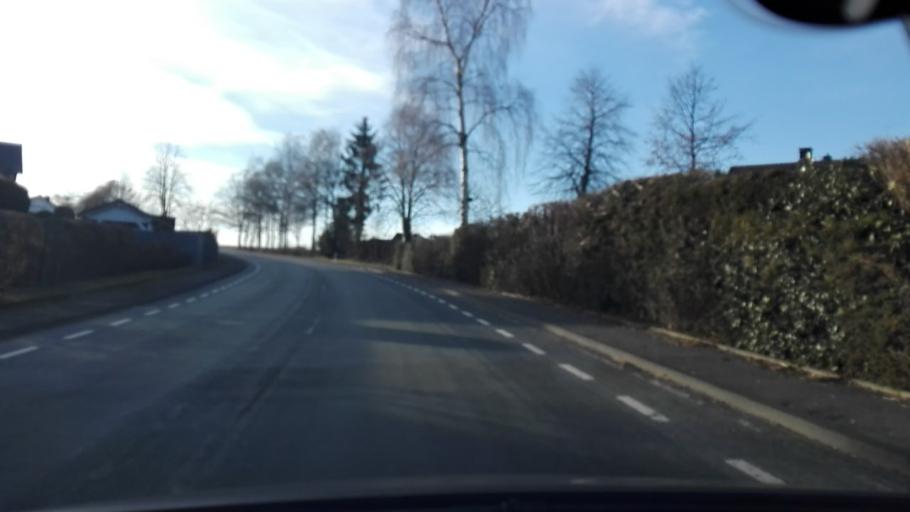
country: DE
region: North Rhine-Westphalia
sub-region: Regierungsbezirk Arnsberg
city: Schmallenberg
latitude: 51.1654
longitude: 8.2270
